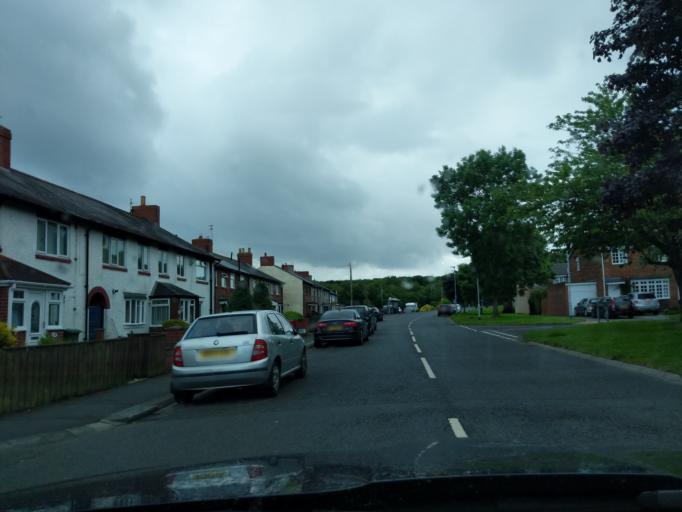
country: GB
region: England
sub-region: Northumberland
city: Seaton Delaval
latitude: 55.0822
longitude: -1.5243
